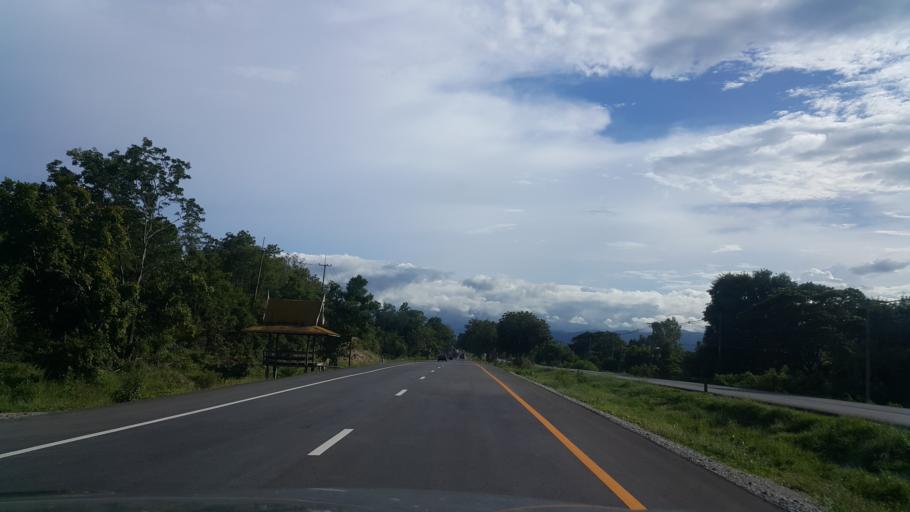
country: TH
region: Tak
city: Ban Tak
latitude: 17.1304
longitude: 99.1028
